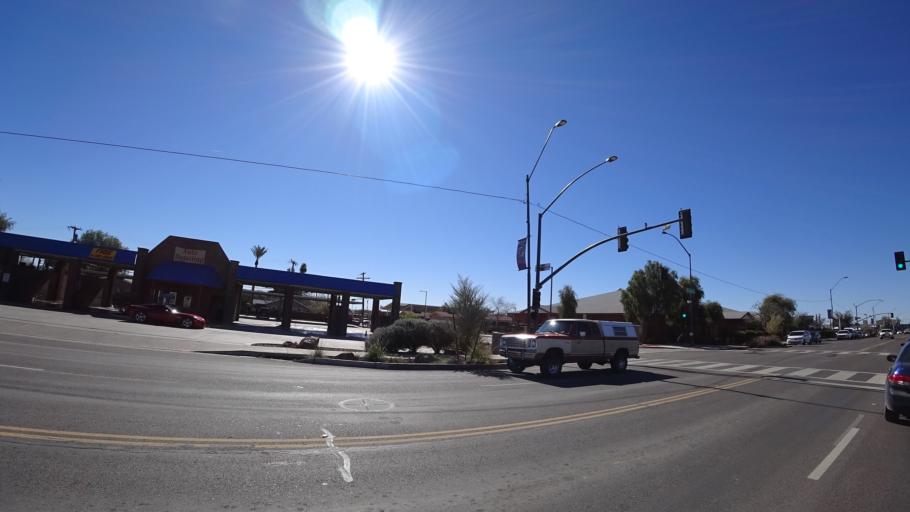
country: US
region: Arizona
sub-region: Maricopa County
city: Buckeye
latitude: 33.3706
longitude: -112.5819
